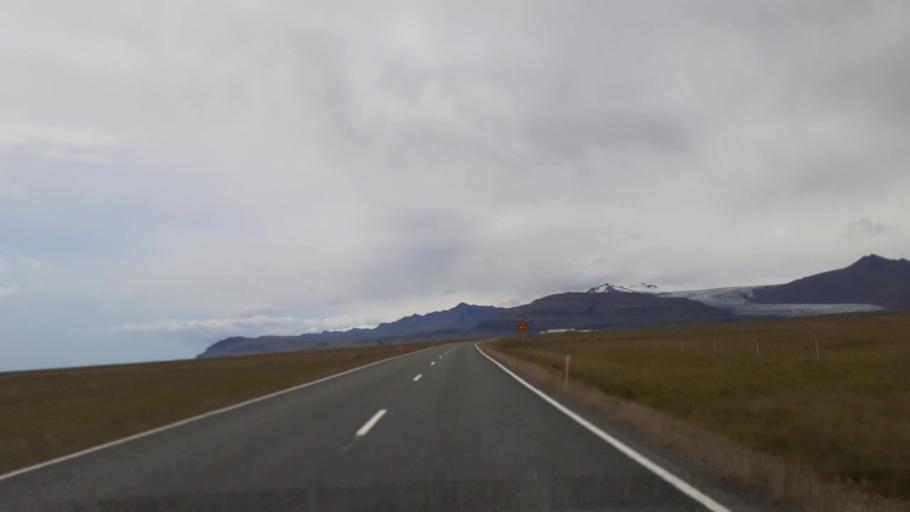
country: IS
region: East
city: Hoefn
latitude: 64.2639
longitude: -15.5172
